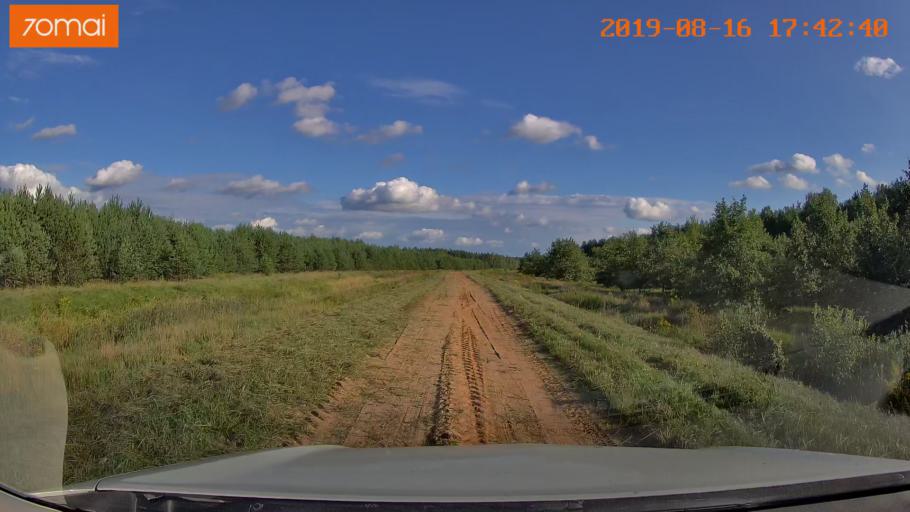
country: BY
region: Mogilev
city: Asipovichy
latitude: 53.2352
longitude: 28.6671
